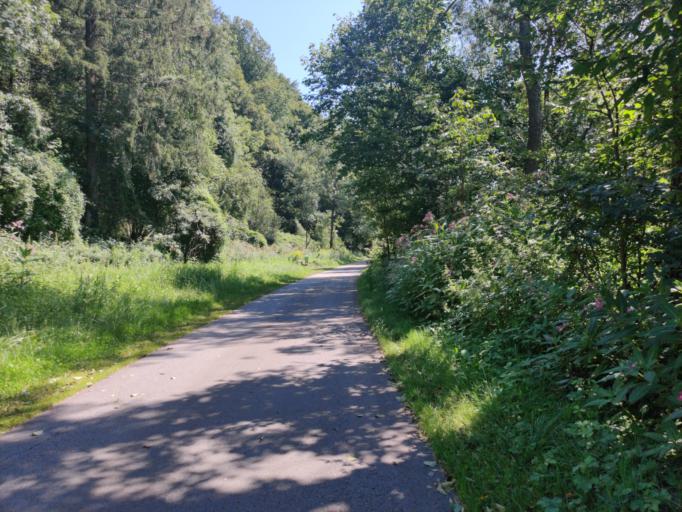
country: AT
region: Upper Austria
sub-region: Politischer Bezirk Rohrbach
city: Pfarrkirchen im Muehlkreis
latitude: 48.4416
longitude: 13.8397
